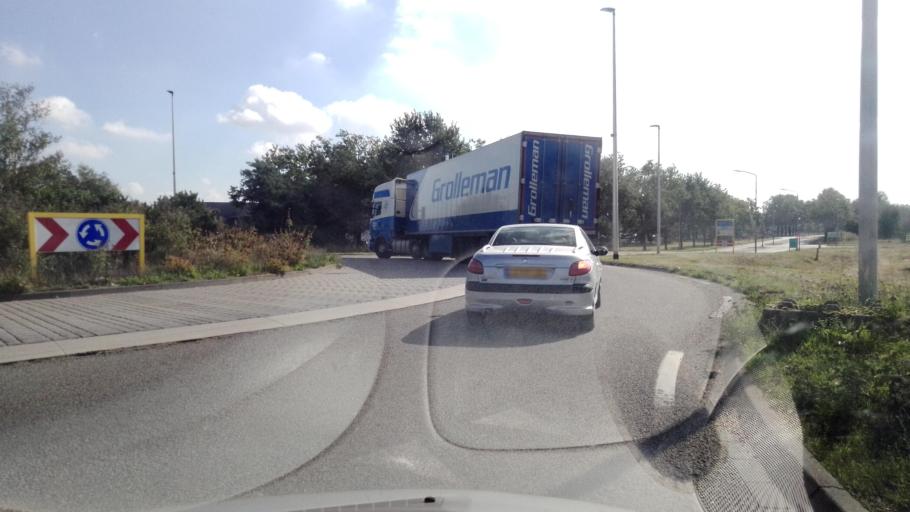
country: NL
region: North Brabant
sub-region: Gemeente Helmond
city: Helmond
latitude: 51.4522
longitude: 5.7002
